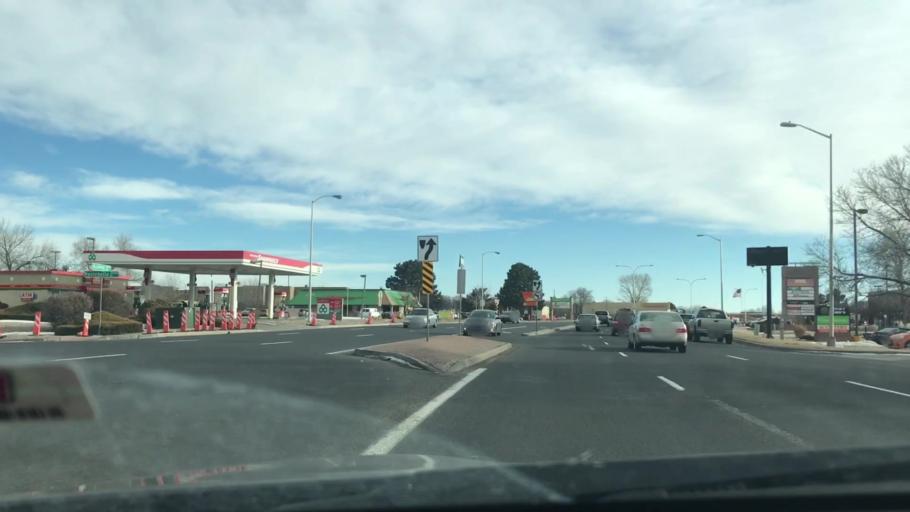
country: US
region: Colorado
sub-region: El Paso County
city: Cimarron Hills
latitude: 38.8943
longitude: -104.7583
